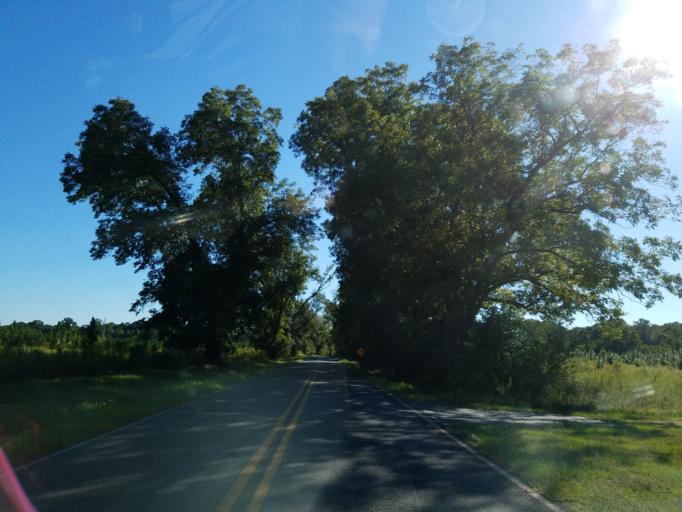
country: US
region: Georgia
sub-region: Dooly County
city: Vienna
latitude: 32.2074
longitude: -83.8989
